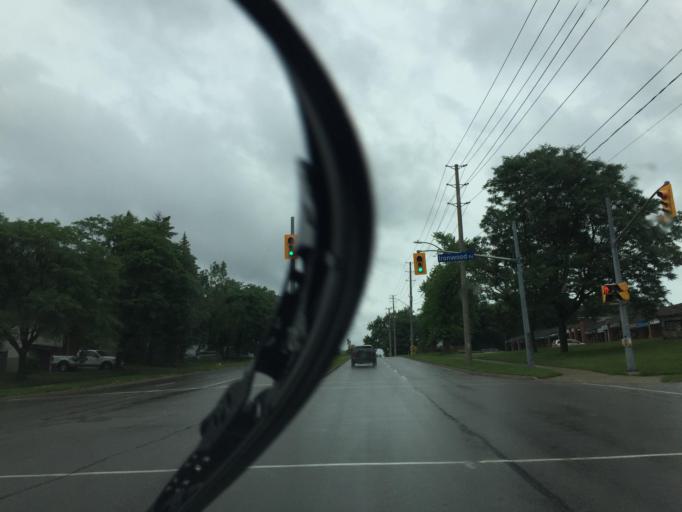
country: CA
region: Ontario
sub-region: Wellington County
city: Guelph
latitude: 43.5081
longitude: -80.2321
